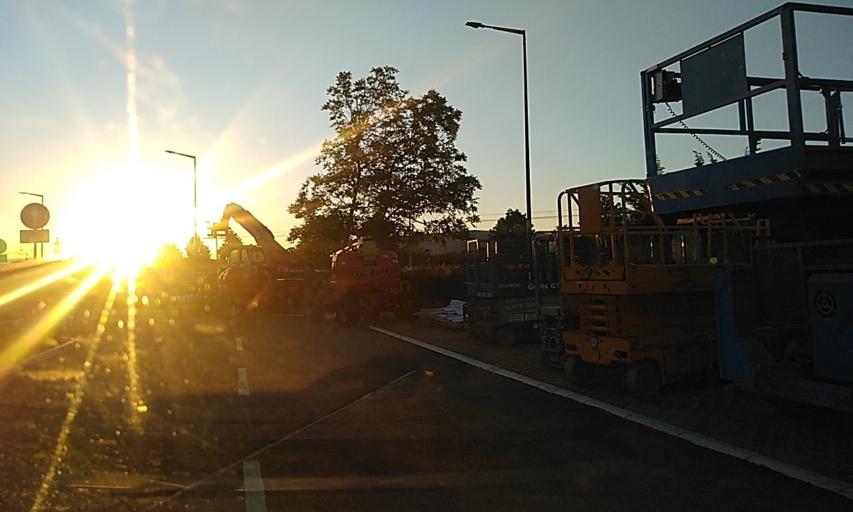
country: RS
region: Central Serbia
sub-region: Nisavski Okrug
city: Nis
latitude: 43.3255
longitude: 21.9121
